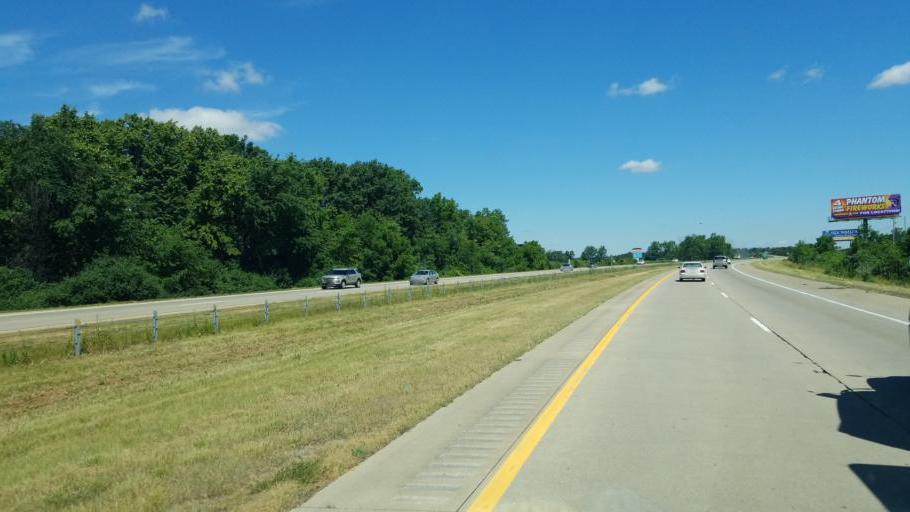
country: US
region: Ohio
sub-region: Lucas County
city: Sylvania
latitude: 41.7383
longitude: -83.6928
